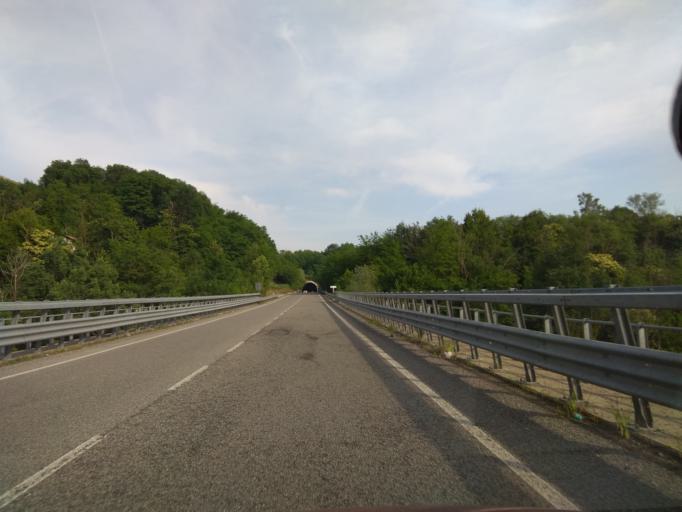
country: IT
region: Piedmont
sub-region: Provincia di Biella
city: Vallanzengo
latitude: 45.6094
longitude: 8.1605
